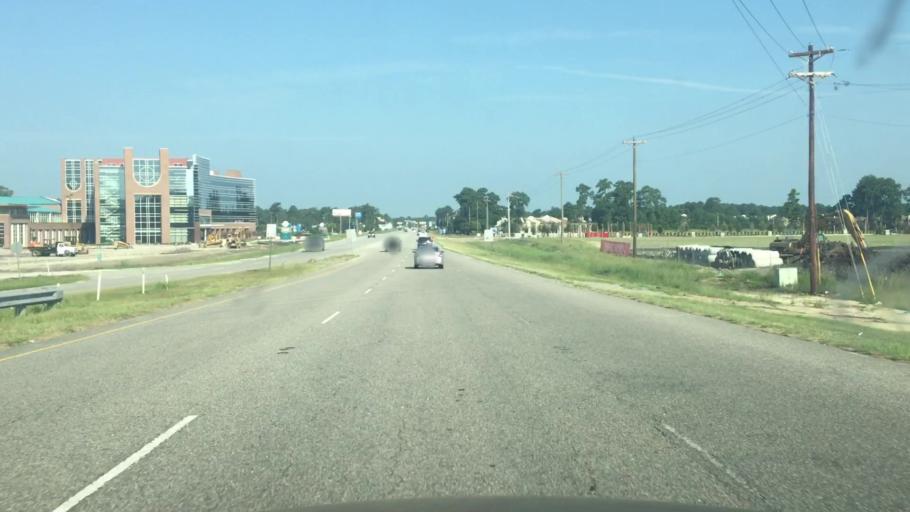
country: US
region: South Carolina
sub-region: Horry County
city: Little River
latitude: 33.8653
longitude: -78.6604
